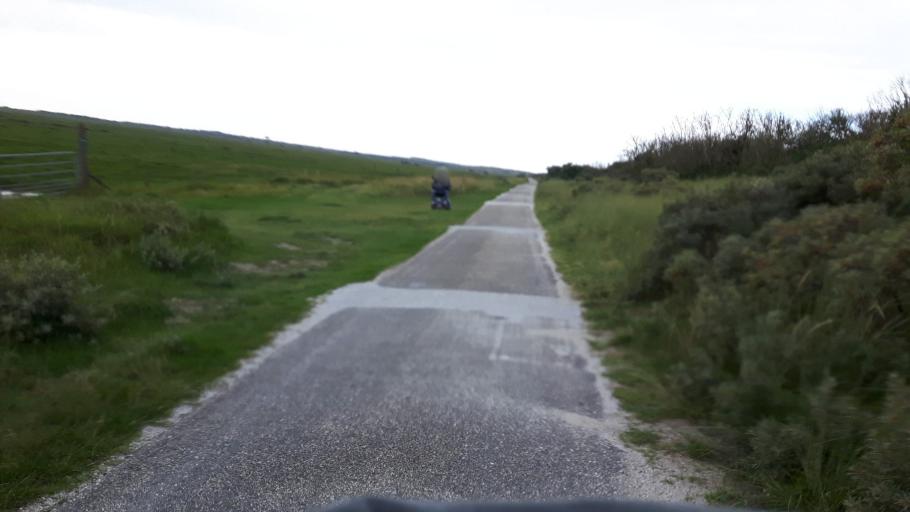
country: NL
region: Friesland
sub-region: Gemeente Ameland
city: Nes
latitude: 53.4609
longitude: 5.8562
